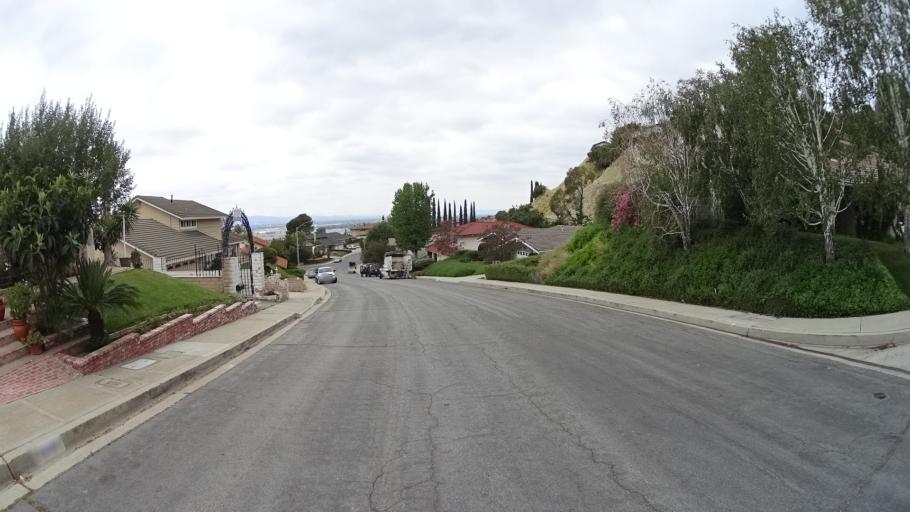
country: US
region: California
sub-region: Los Angeles County
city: Burbank
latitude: 34.2126
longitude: -118.3291
